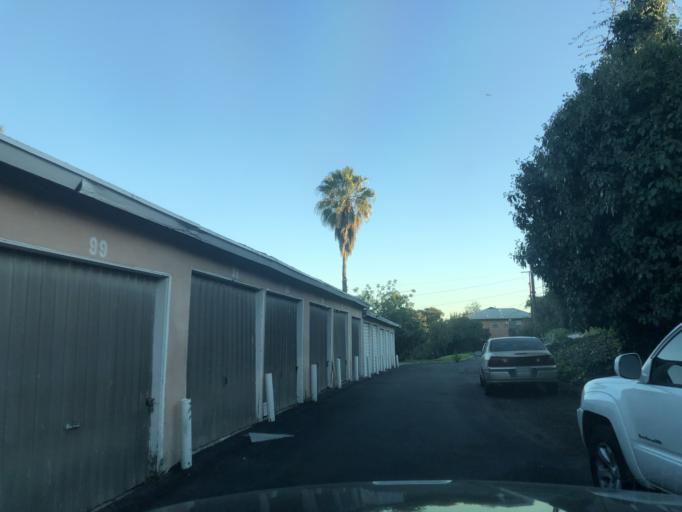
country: US
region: California
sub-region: Los Angeles County
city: Ladera Heights
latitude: 33.9894
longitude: -118.3618
